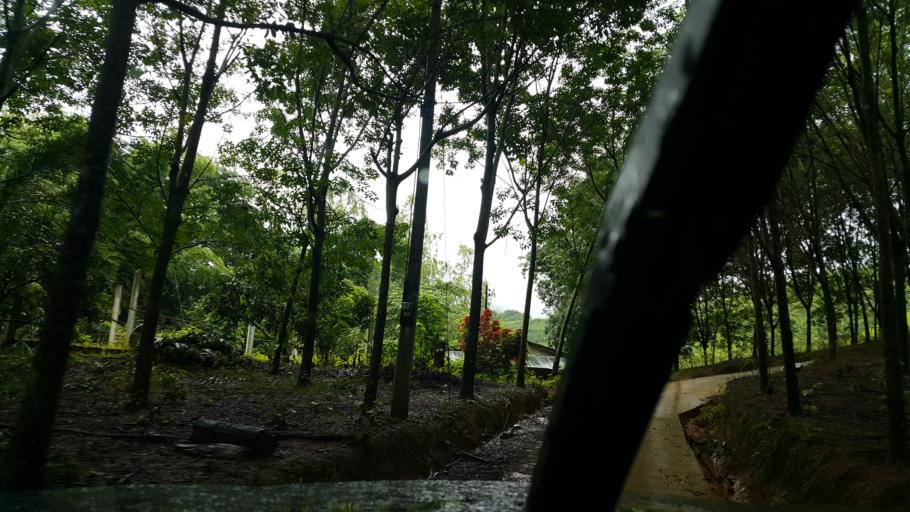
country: TH
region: Phayao
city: Chiang Kham
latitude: 19.4983
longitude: 100.4645
